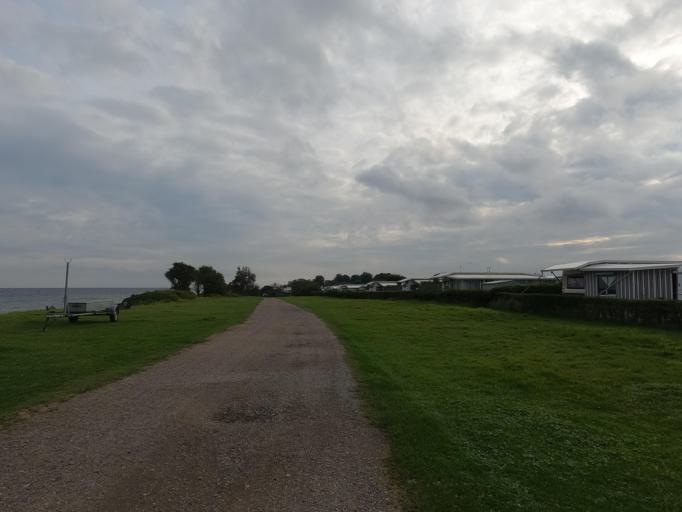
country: DE
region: Schleswig-Holstein
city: Grossenbrode
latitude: 54.3309
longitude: 11.0720
